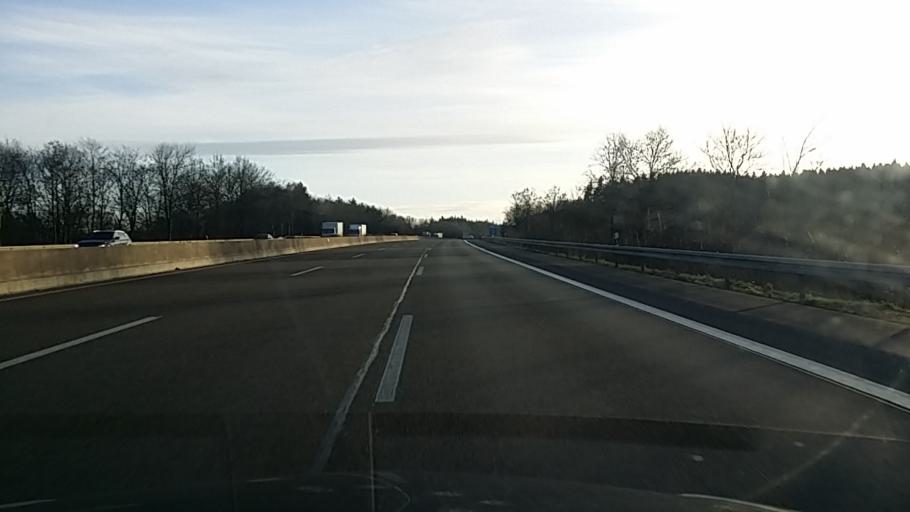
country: DE
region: Hesse
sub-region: Regierungsbezirk Kassel
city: Burghaun
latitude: 50.6890
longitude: 9.6833
